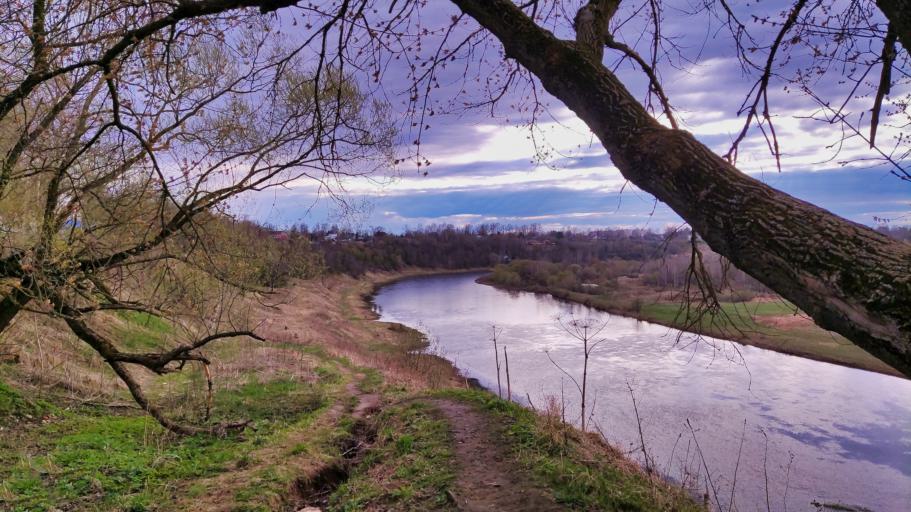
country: RU
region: Tverskaya
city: Rzhev
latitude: 56.2532
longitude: 34.3135
